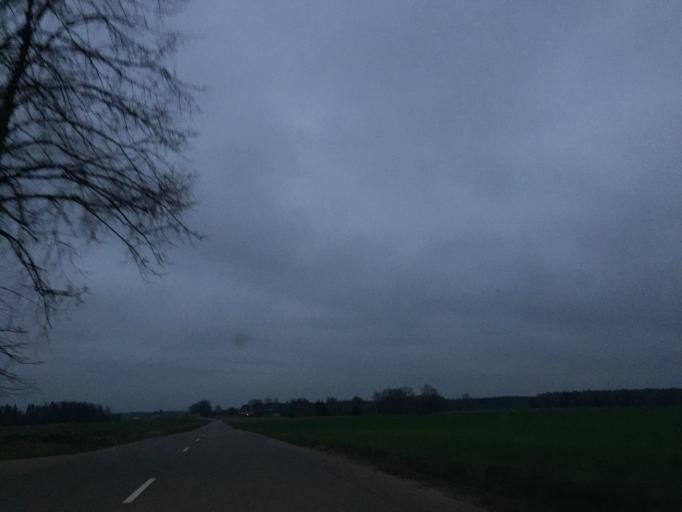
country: LV
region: Koceni
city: Koceni
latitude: 57.5481
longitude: 25.2873
